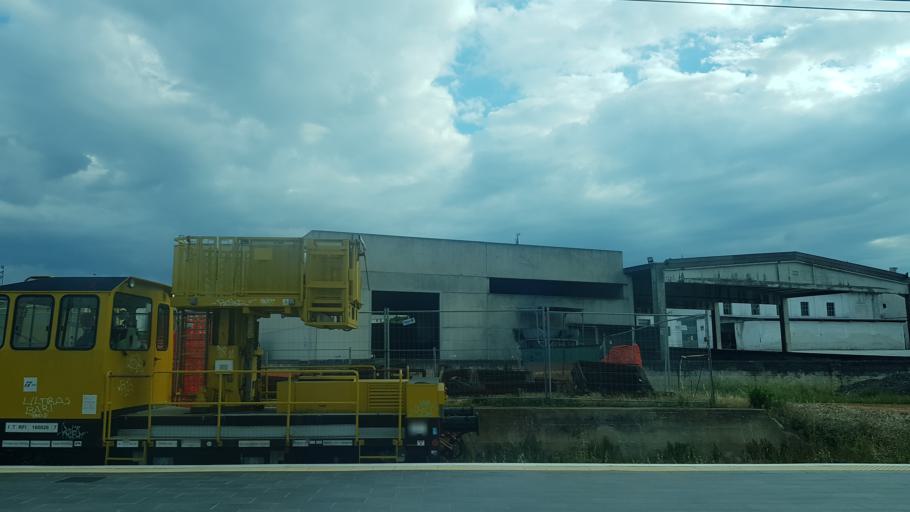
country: IT
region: Apulia
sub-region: Provincia di Brindisi
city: Ostuni
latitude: 40.7528
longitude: 17.5791
